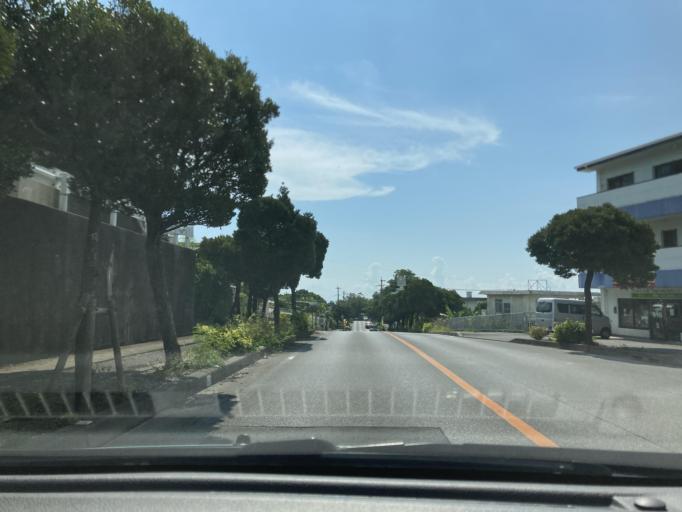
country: JP
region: Okinawa
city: Tomigusuku
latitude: 26.1448
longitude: 127.7645
